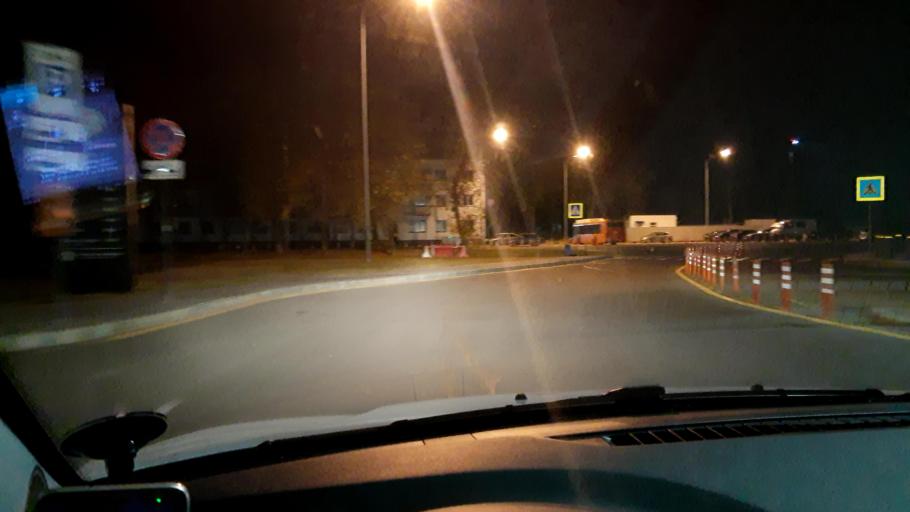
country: RU
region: Nizjnij Novgorod
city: Gorbatovka
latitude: 56.2191
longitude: 43.7918
